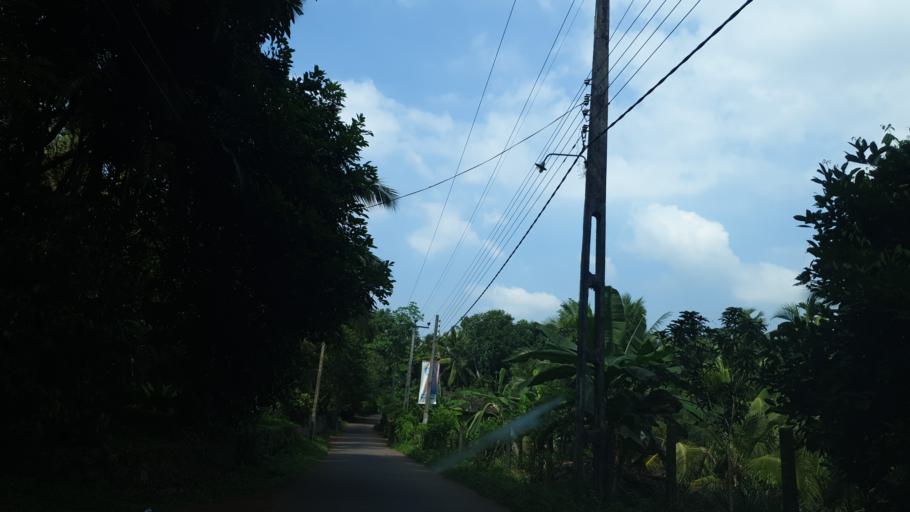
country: LK
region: Western
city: Panadura
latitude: 6.7291
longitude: 79.9535
